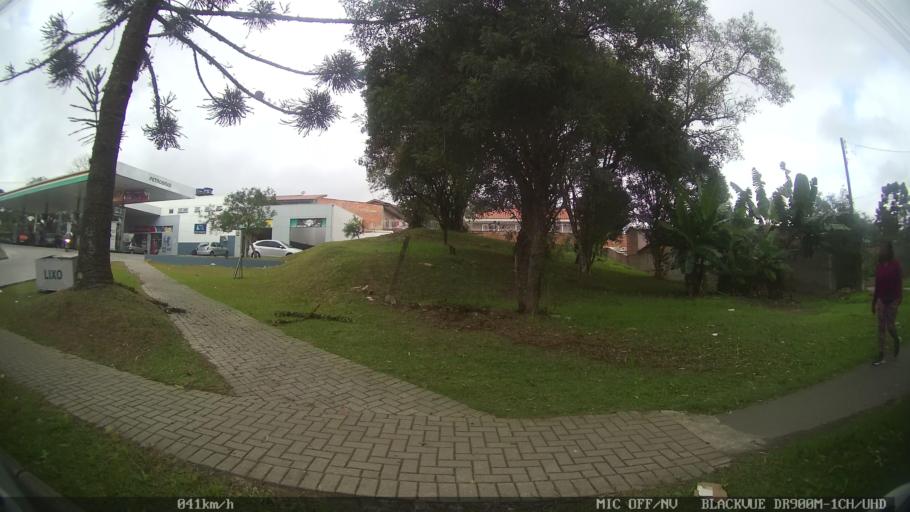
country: BR
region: Parana
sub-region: Almirante Tamandare
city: Almirante Tamandare
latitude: -25.3602
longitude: -49.2483
